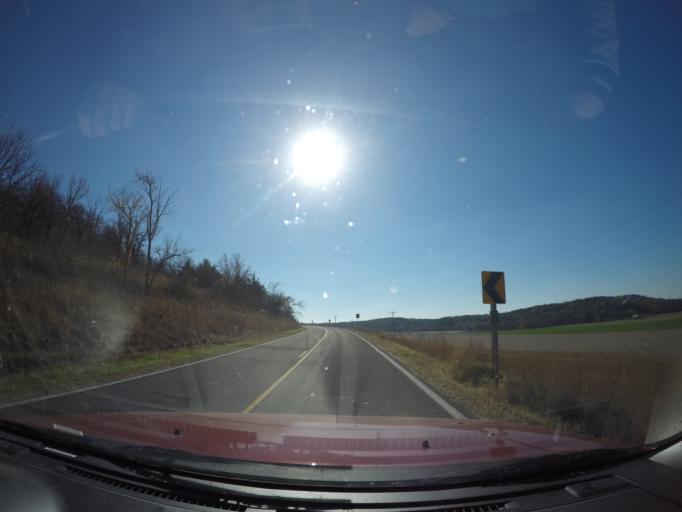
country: US
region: Kansas
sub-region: Geary County
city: Grandview Plaza
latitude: 38.9959
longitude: -96.7305
